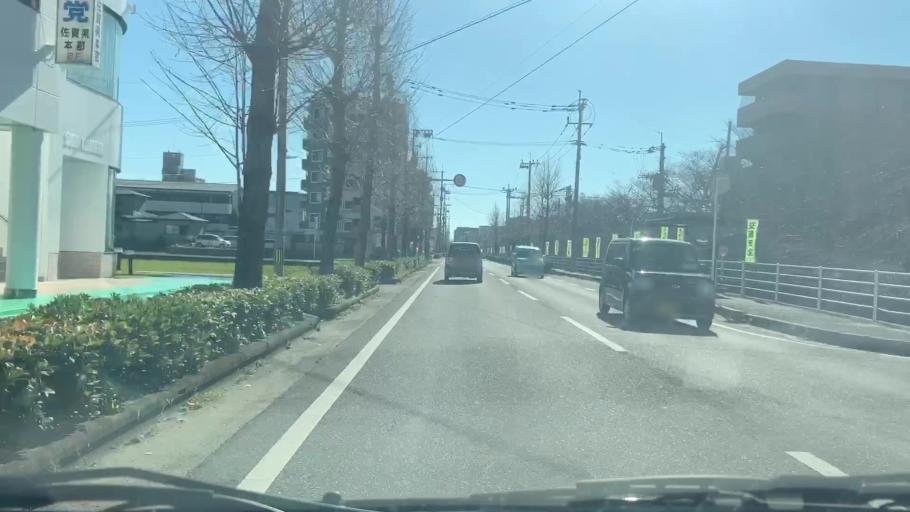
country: JP
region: Saga Prefecture
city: Saga-shi
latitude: 33.2870
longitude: 130.2683
